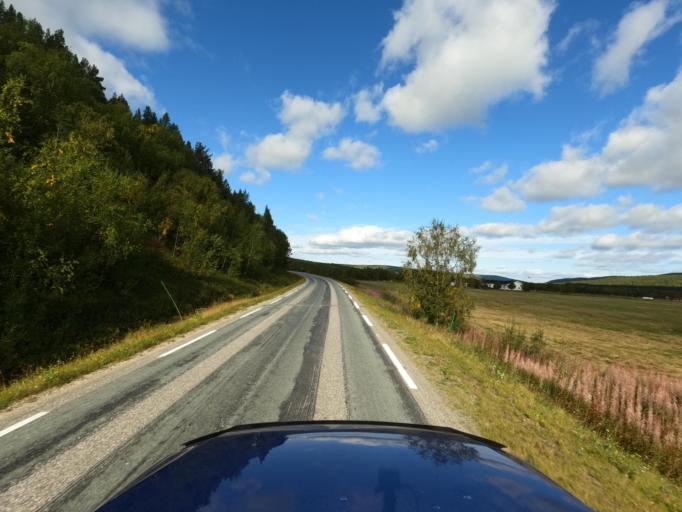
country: NO
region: Finnmark Fylke
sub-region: Karasjok
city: Karasjohka
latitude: 69.4112
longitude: 25.8046
